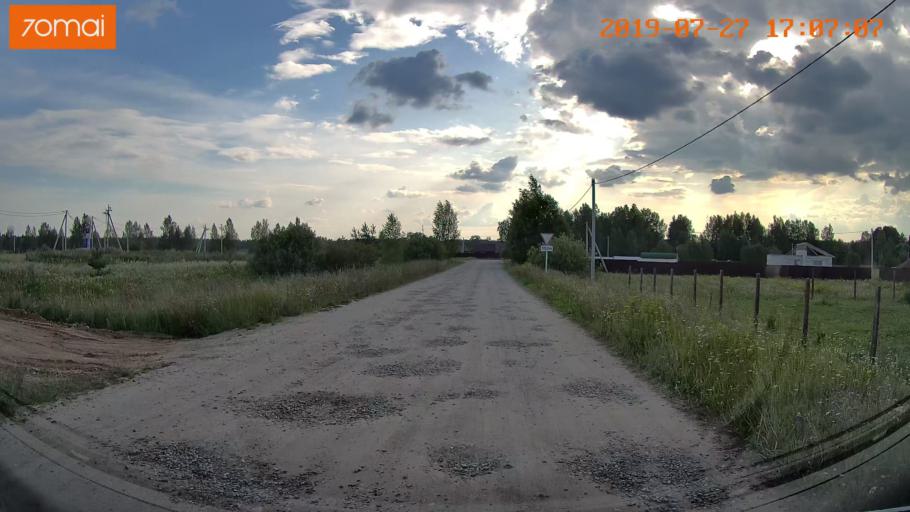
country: RU
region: Ivanovo
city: Novo-Talitsy
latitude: 57.0852
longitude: 40.8376
